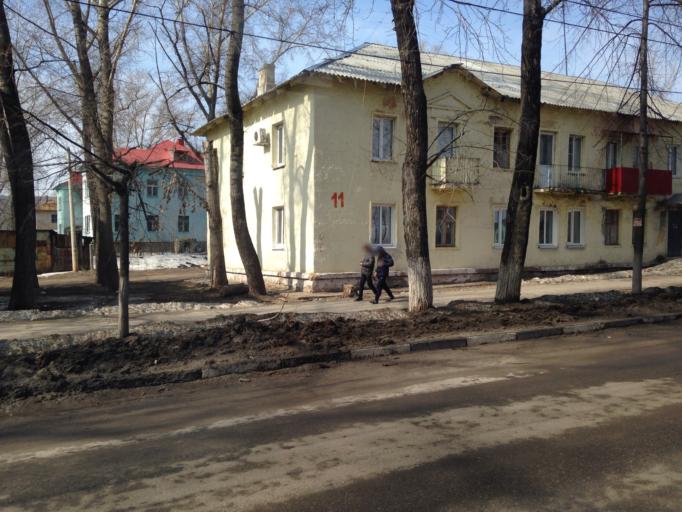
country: RU
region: Ulyanovsk
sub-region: Ulyanovskiy Rayon
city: Ulyanovsk
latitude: 54.3395
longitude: 48.5494
